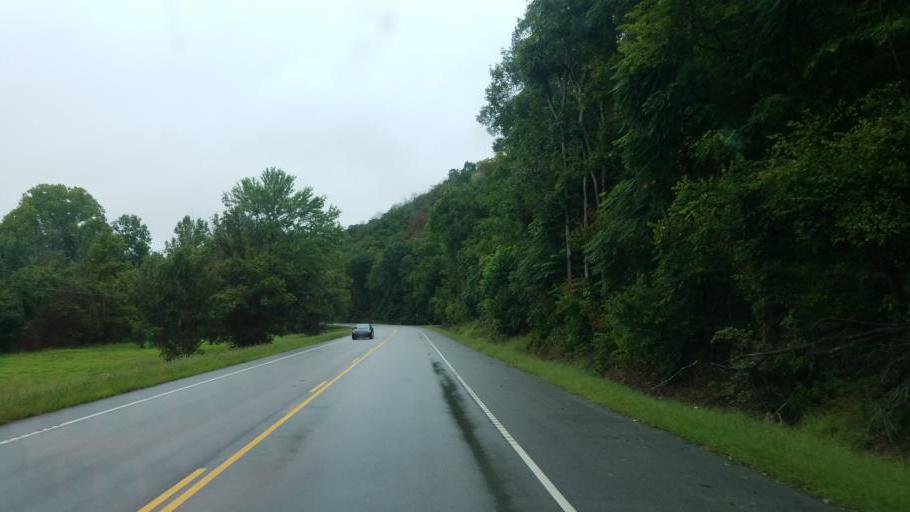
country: US
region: Ohio
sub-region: Adams County
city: Manchester
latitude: 38.6726
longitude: -83.6363
